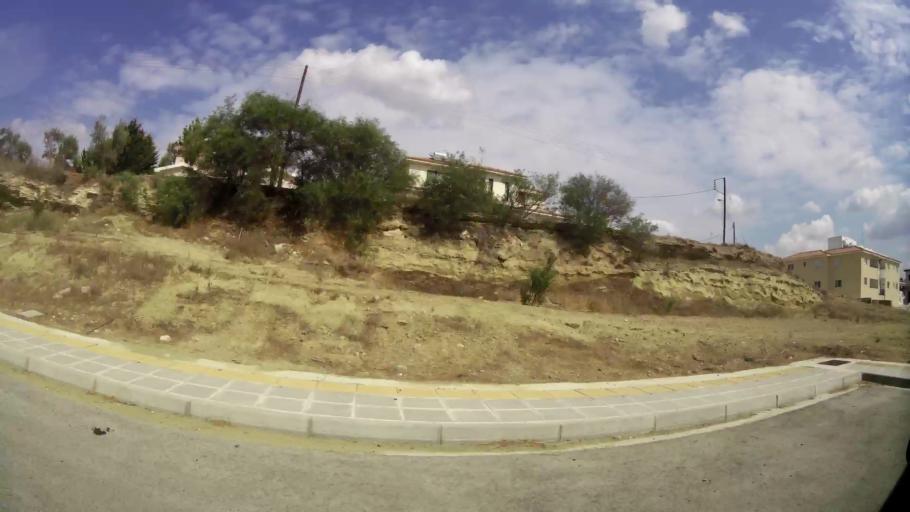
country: CY
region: Lefkosia
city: Tseri
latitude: 35.0712
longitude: 33.3306
